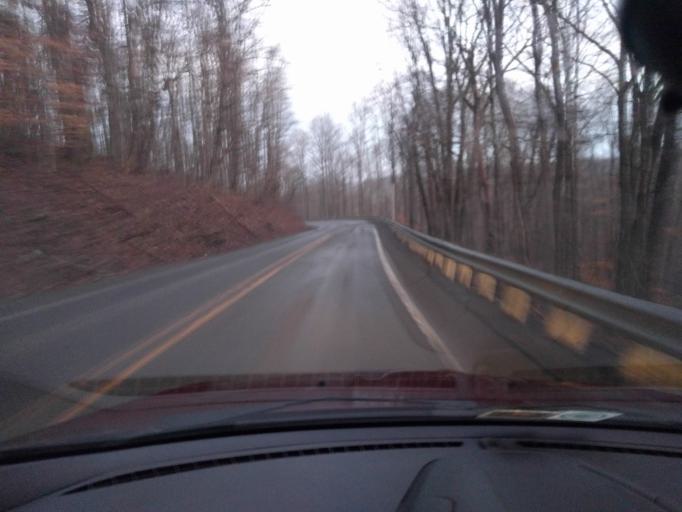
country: US
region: West Virginia
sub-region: Greenbrier County
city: Rainelle
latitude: 37.9879
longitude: -80.8551
